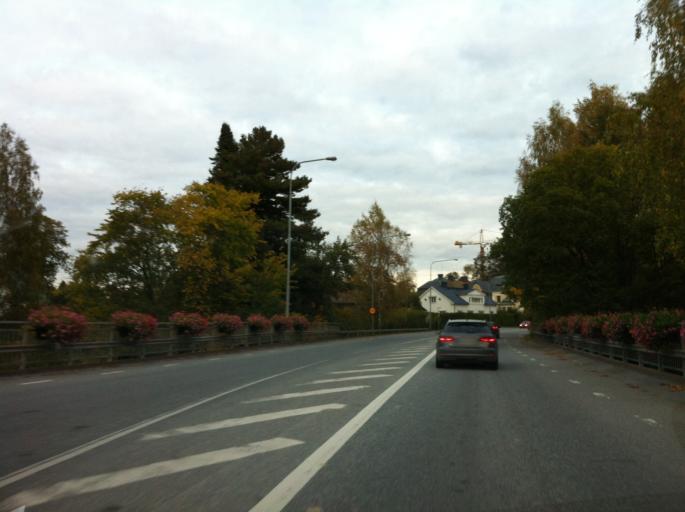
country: SE
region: OErebro
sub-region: Nora Kommun
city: Nora
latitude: 59.5005
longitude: 15.0337
